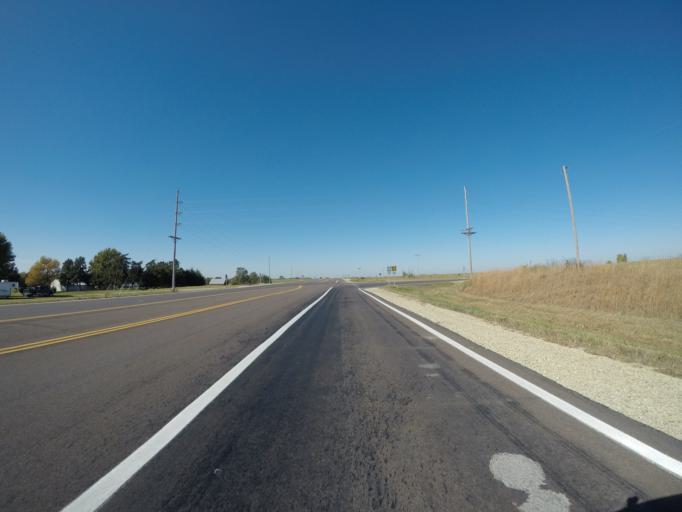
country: US
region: Kansas
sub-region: Clay County
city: Clay Center
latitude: 39.3071
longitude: -96.9229
